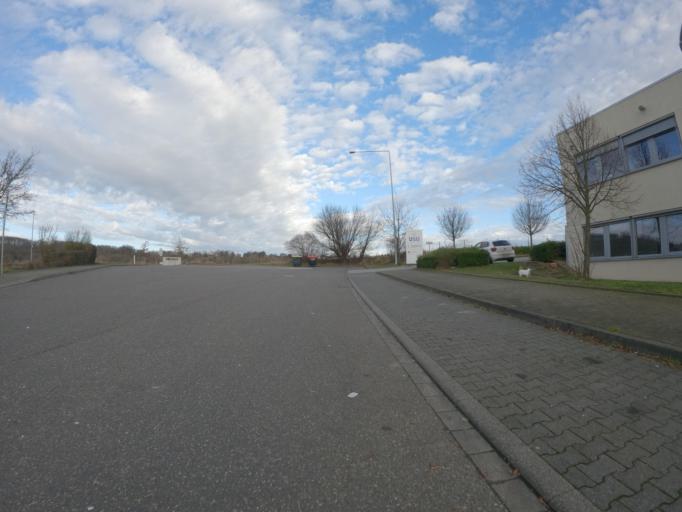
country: DE
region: North Rhine-Westphalia
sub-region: Regierungsbezirk Koln
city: Wurselen
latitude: 50.7907
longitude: 6.1424
